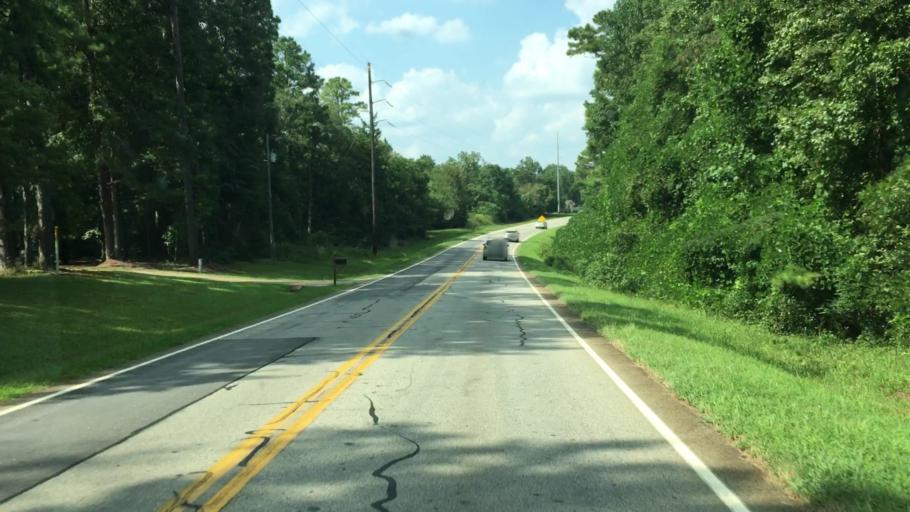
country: US
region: Georgia
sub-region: Jasper County
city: Monticello
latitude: 33.2812
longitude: -83.7135
